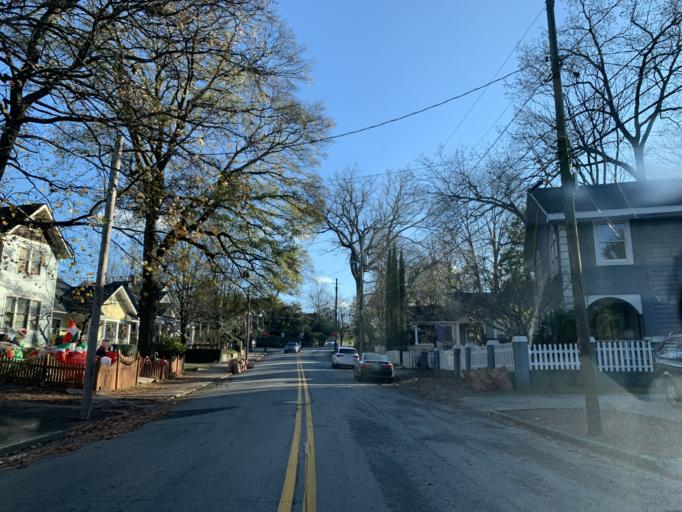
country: US
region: Georgia
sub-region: Fulton County
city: Atlanta
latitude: 33.7420
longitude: -84.3793
